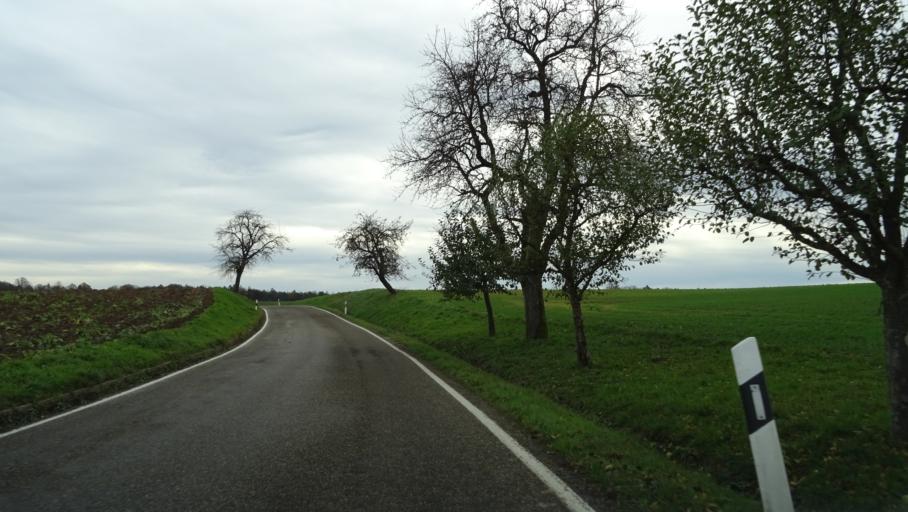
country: DE
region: Baden-Wuerttemberg
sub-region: Karlsruhe Region
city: Neckargerach
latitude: 49.3911
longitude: 9.0982
